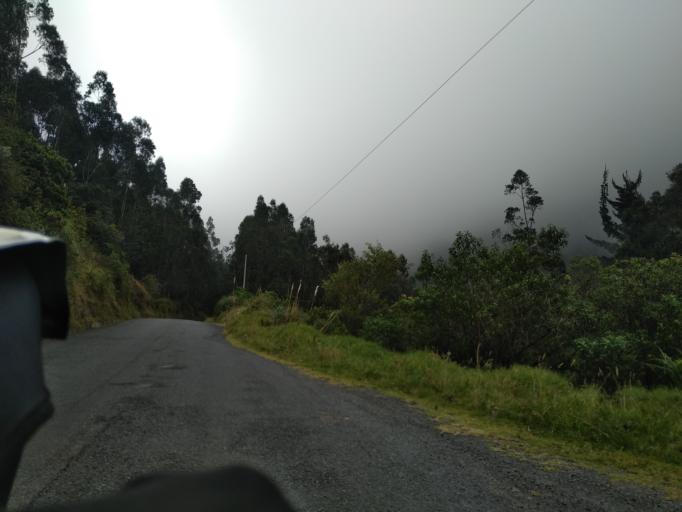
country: EC
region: Cotopaxi
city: Saquisili
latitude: -0.6929
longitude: -78.8203
